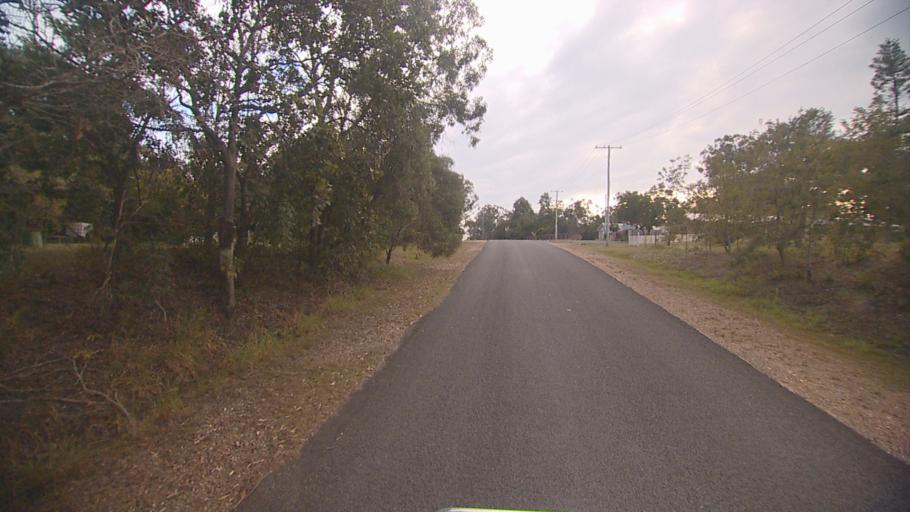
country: AU
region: Queensland
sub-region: Logan
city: Logan Reserve
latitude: -27.7452
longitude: 153.1382
